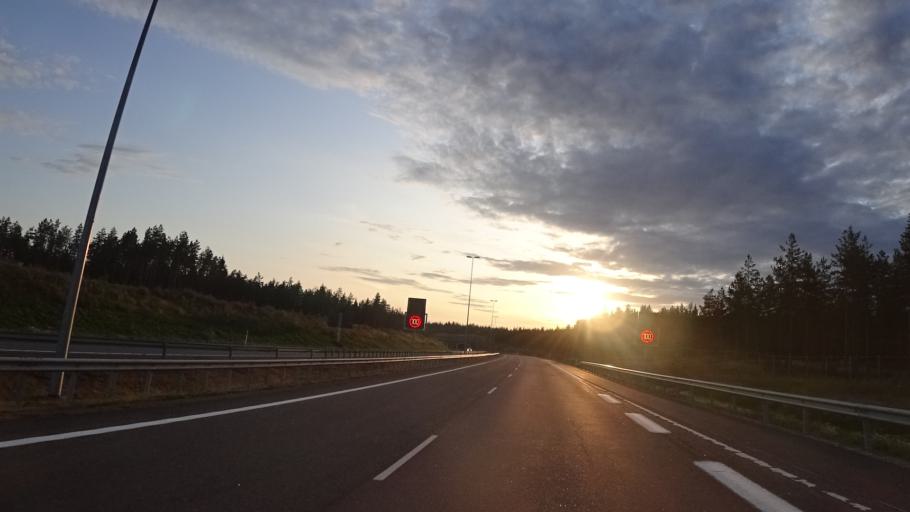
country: FI
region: Kymenlaakso
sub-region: Kotka-Hamina
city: Virojoki
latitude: 60.6124
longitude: 27.8050
